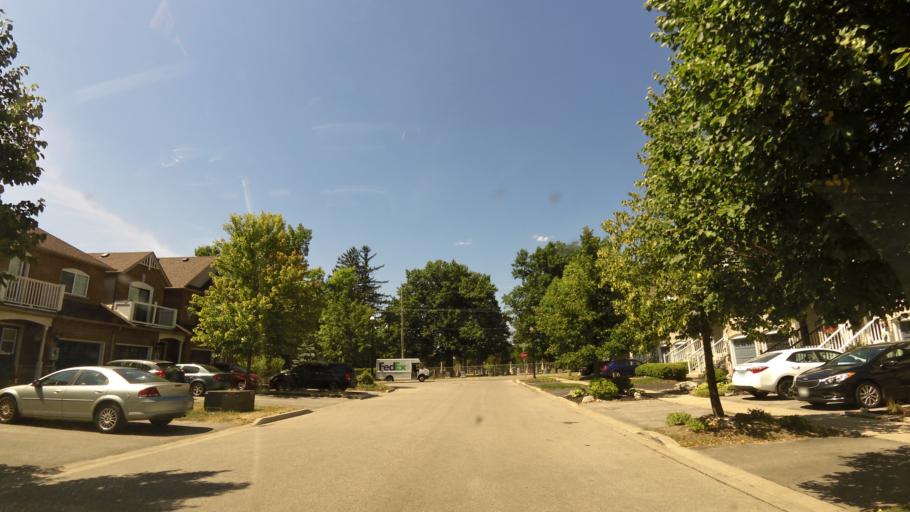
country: CA
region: Ontario
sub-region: Halton
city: Milton
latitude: 43.6534
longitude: -79.9117
